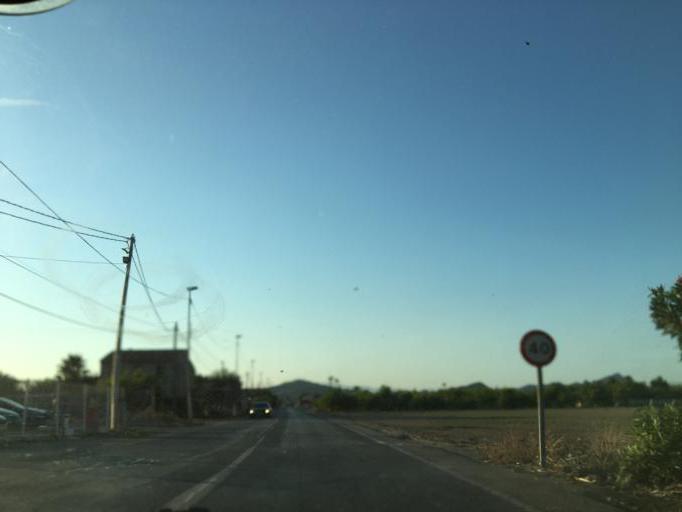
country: ES
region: Murcia
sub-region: Murcia
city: Murcia
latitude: 38.0023
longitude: -1.0768
